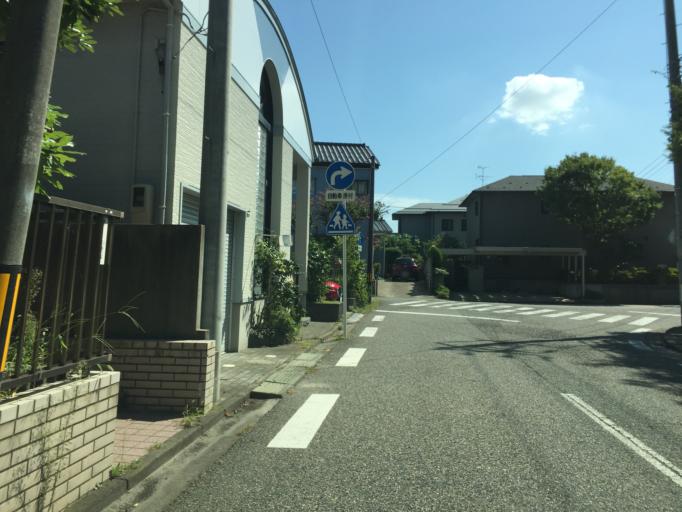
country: JP
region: Niigata
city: Niigata-shi
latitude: 37.9170
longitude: 139.0269
